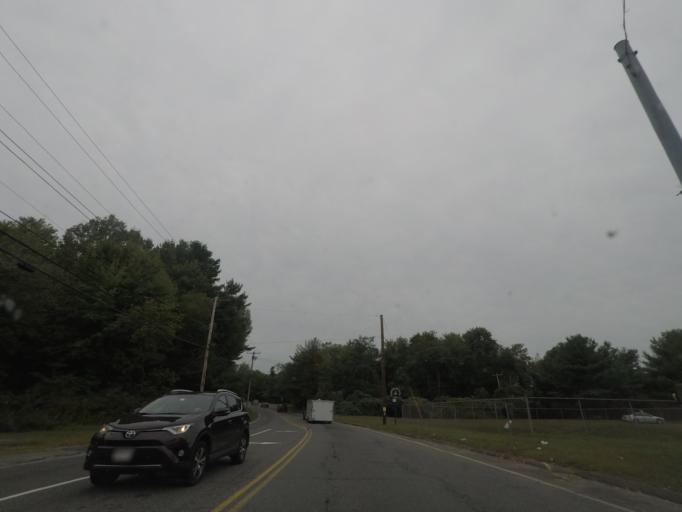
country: US
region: Massachusetts
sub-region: Hampden County
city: Palmer
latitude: 42.1733
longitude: -72.3244
